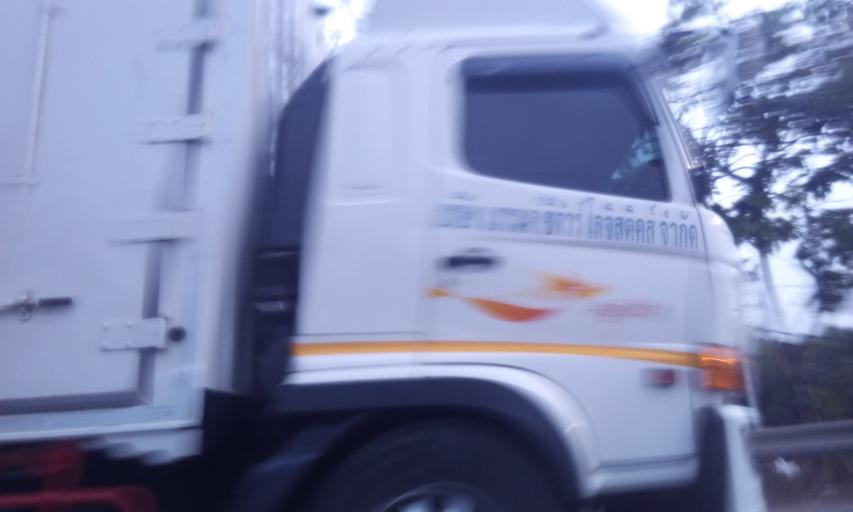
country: TH
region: Chachoengsao
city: Chachoengsao
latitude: 13.6591
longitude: 101.0652
